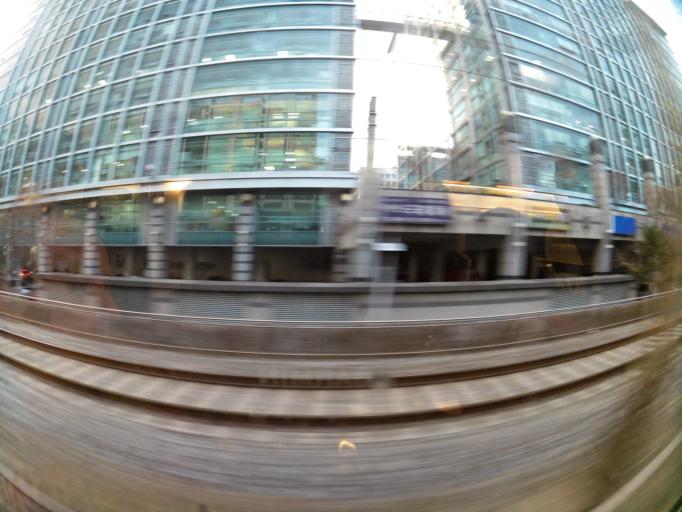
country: KR
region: Gyeonggi-do
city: Kwangmyong
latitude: 37.4795
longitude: 126.8834
